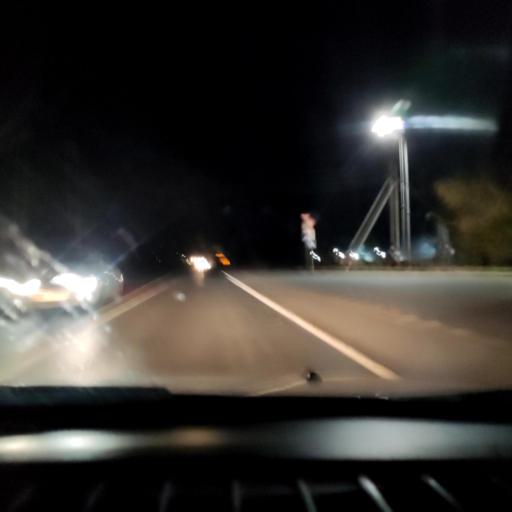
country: RU
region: Samara
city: Tol'yatti
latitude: 53.5750
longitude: 49.3394
